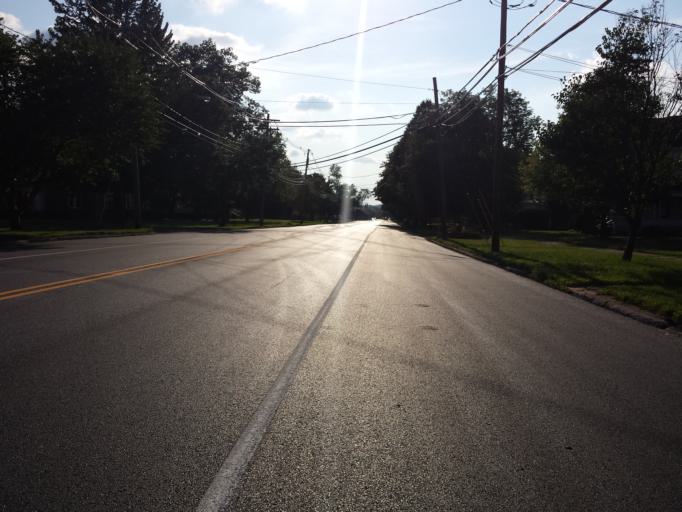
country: US
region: New York
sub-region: St. Lawrence County
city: Potsdam
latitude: 44.6699
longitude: -74.9764
